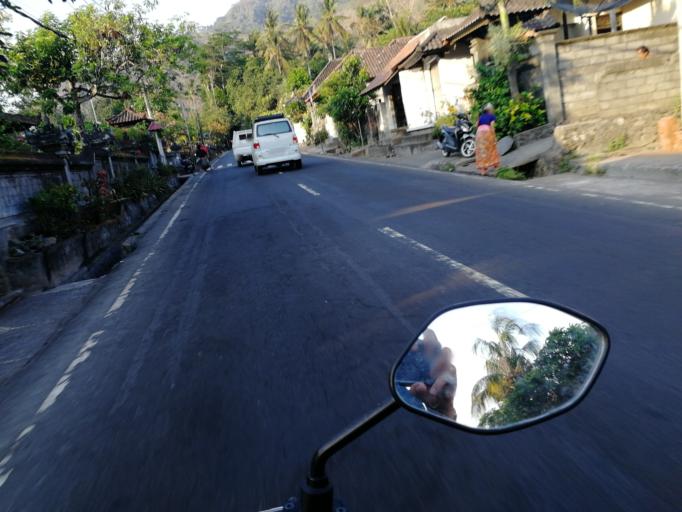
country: ID
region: Bali
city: Banjar Buayang
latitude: -8.3515
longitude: 115.6142
